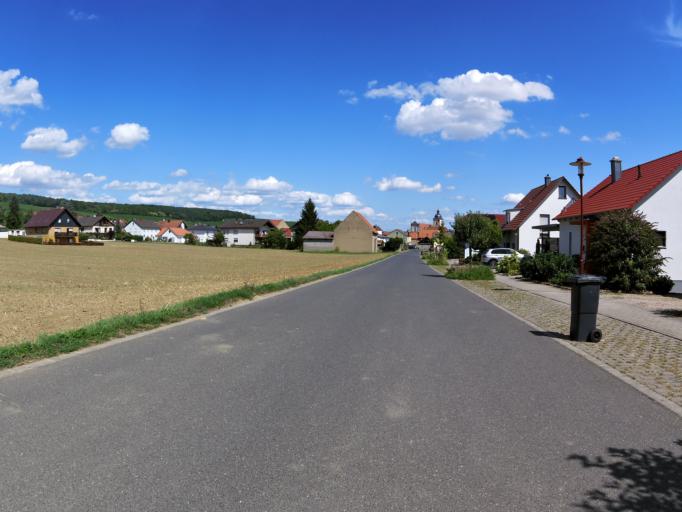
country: DE
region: Bavaria
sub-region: Regierungsbezirk Unterfranken
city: Prosselsheim
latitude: 49.8809
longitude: 10.1548
